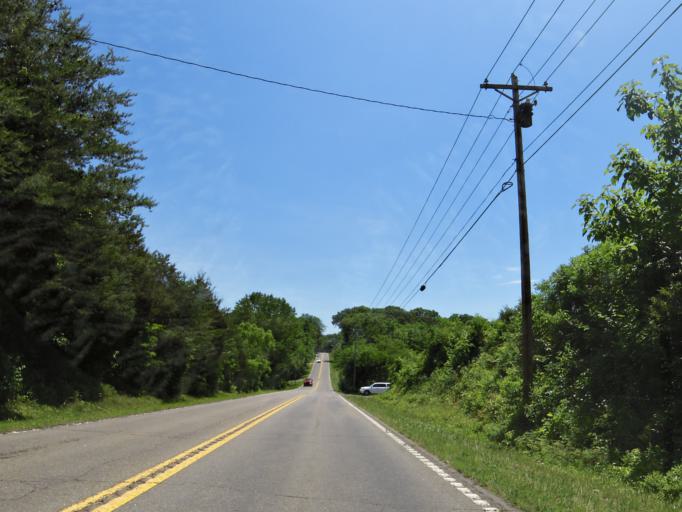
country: US
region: Tennessee
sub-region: Jefferson County
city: Dandridge
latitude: 36.0212
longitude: -83.4451
